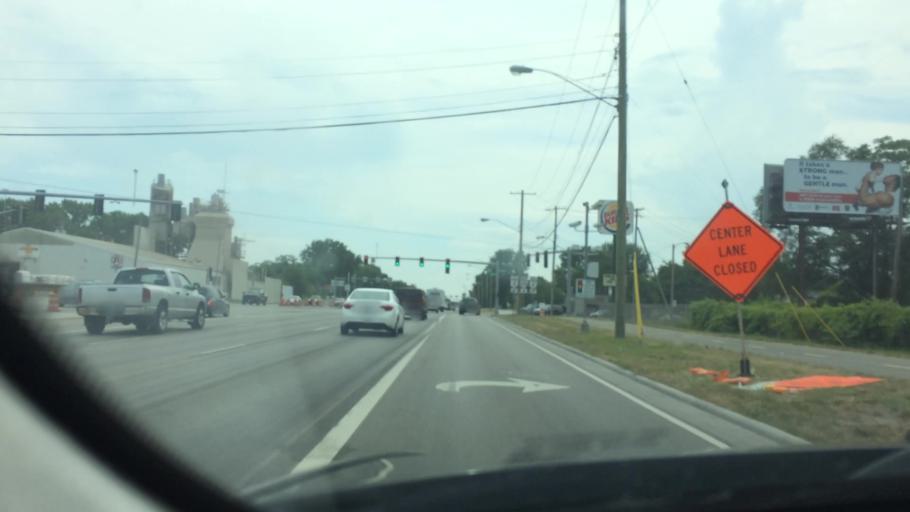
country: US
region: Ohio
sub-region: Wood County
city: Rossford
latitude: 41.6351
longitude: -83.5609
